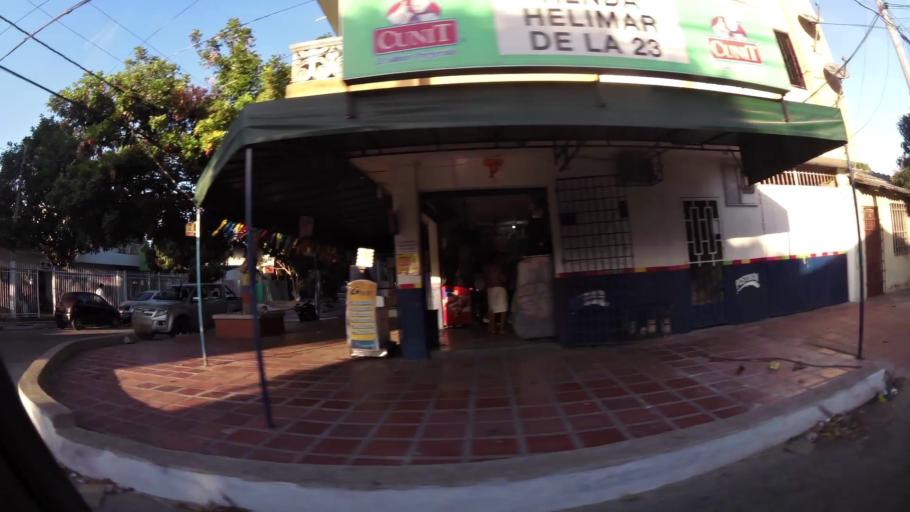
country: CO
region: Atlantico
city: Barranquilla
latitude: 10.9693
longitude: -74.7986
